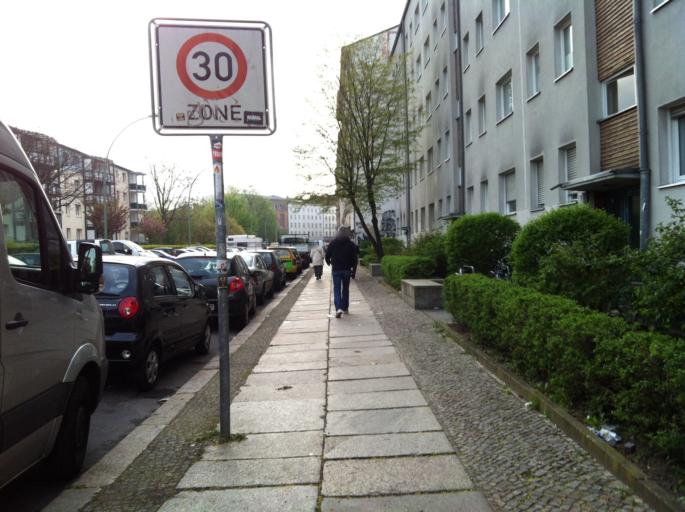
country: DE
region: Berlin
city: Bezirk Kreuzberg
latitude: 52.5050
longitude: 13.4116
